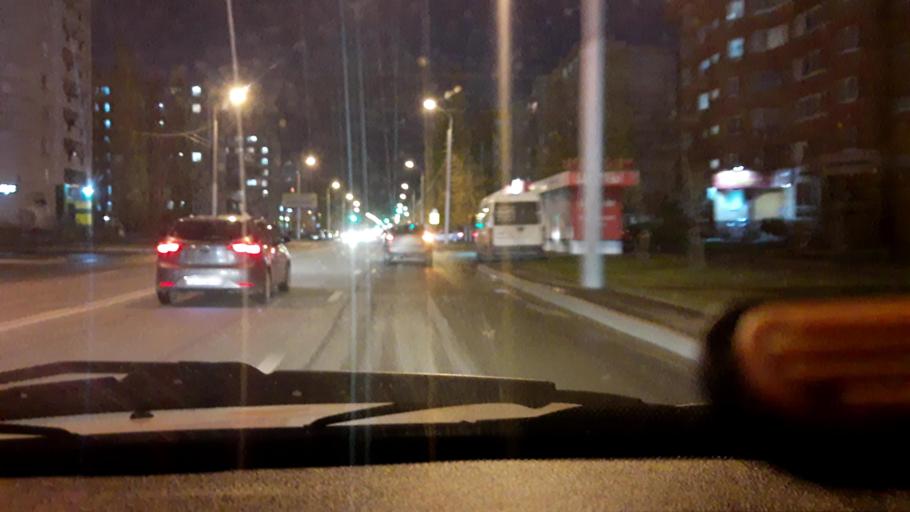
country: RU
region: Bashkortostan
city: Ufa
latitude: 54.7647
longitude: 56.0517
